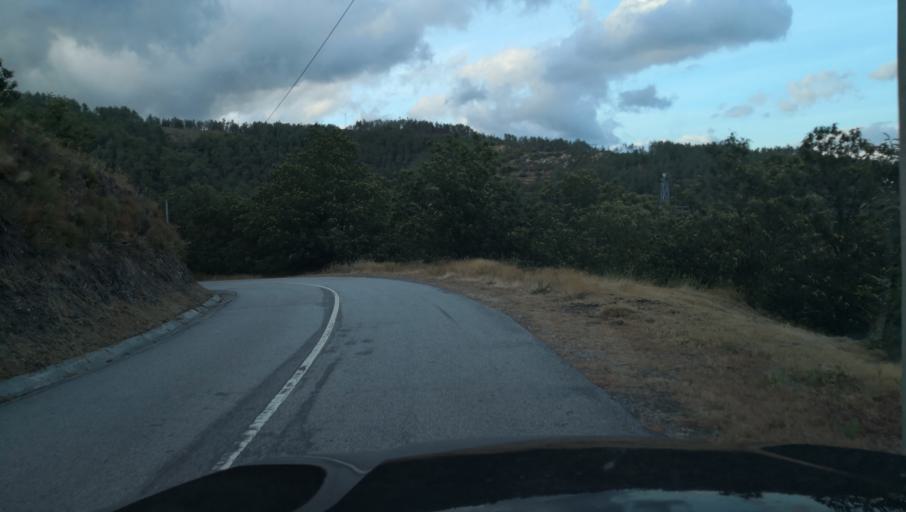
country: PT
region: Vila Real
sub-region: Santa Marta de Penaguiao
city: Santa Marta de Penaguiao
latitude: 41.2399
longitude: -7.8504
